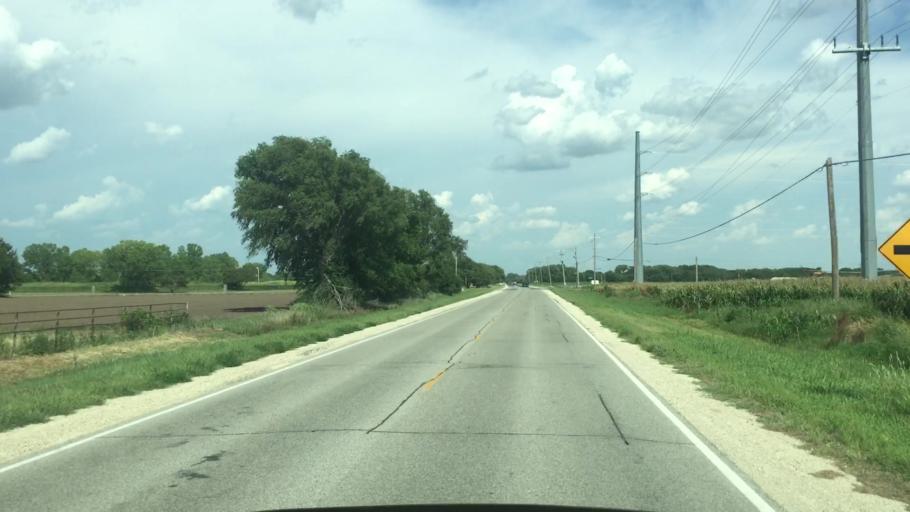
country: US
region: Kansas
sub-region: Sedgwick County
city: Maize
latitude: 37.7810
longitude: -97.4472
